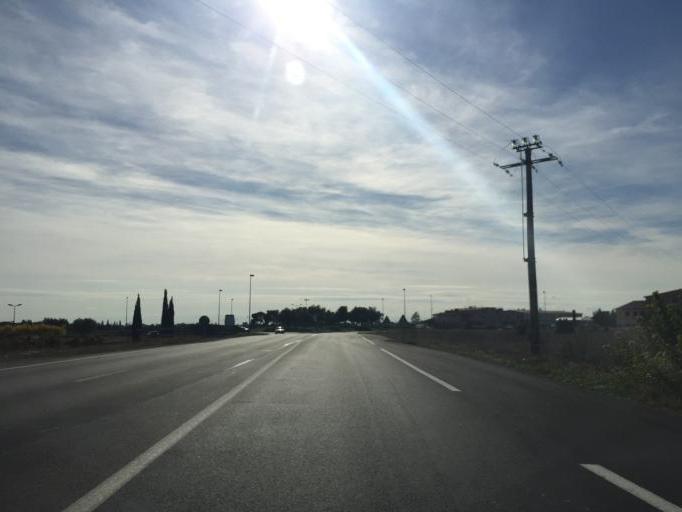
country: FR
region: Rhone-Alpes
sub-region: Departement de la Drome
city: Donzere
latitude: 44.4313
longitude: 4.7133
